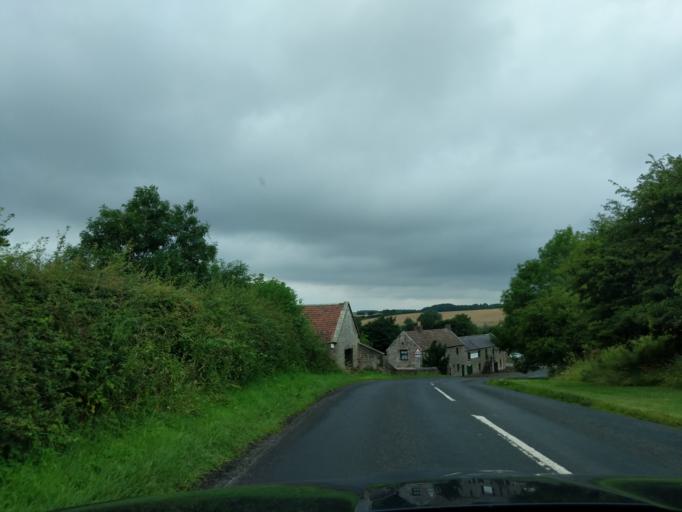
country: GB
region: England
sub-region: Northumberland
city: Ford
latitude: 55.6391
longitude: -2.1055
